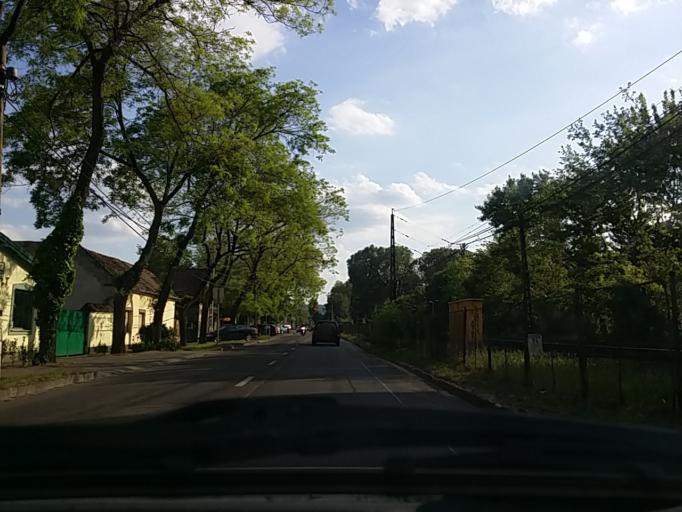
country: HU
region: Pest
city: Budakalasz
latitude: 47.5878
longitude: 19.0464
